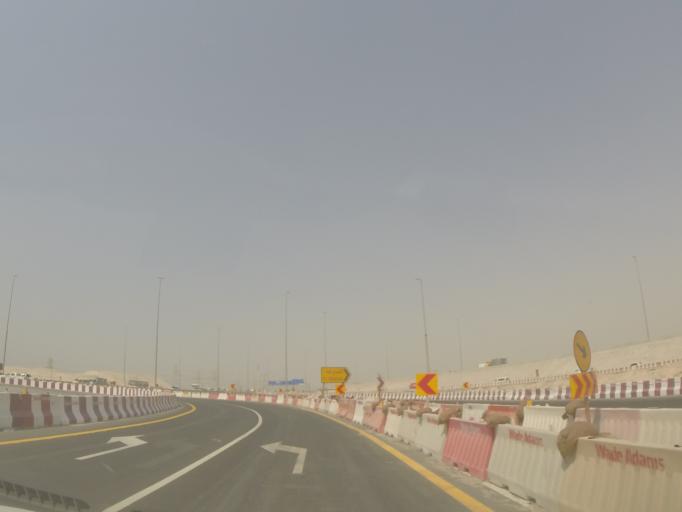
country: AE
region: Dubai
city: Dubai
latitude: 25.0206
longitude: 55.1613
